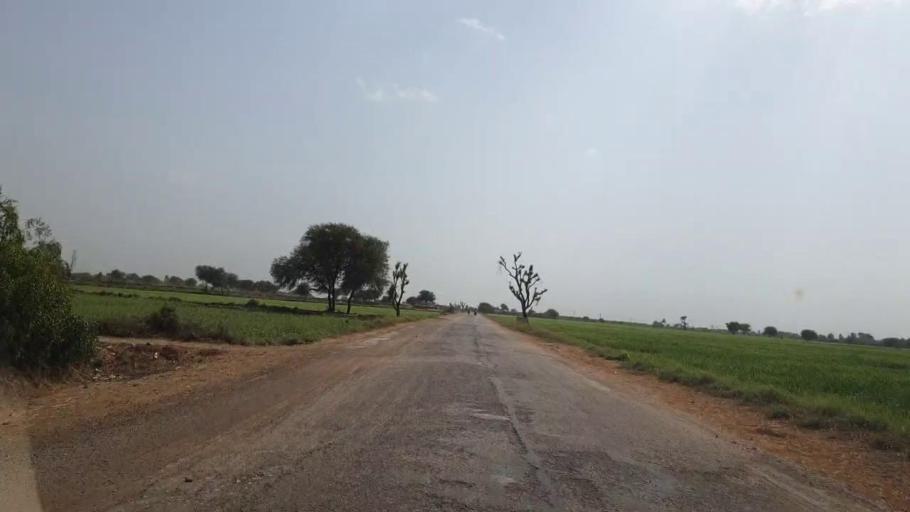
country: PK
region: Sindh
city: Tando Ghulam Ali
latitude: 25.0713
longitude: 68.8230
